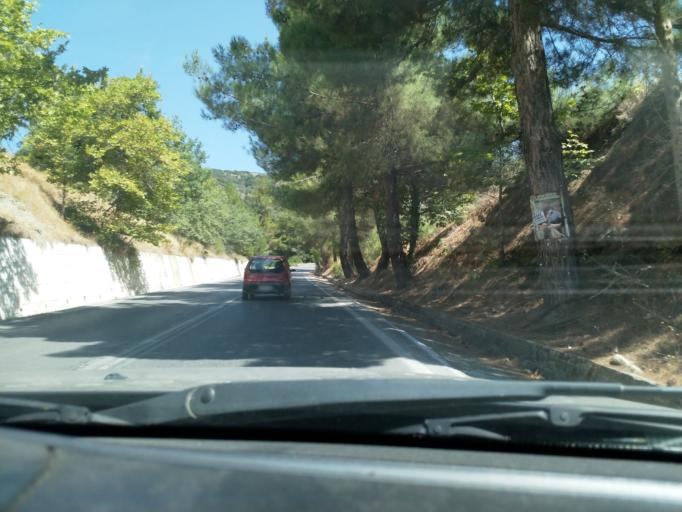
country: GR
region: Crete
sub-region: Nomos Rethymnis
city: Agia Foteini
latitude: 35.2201
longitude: 24.5250
